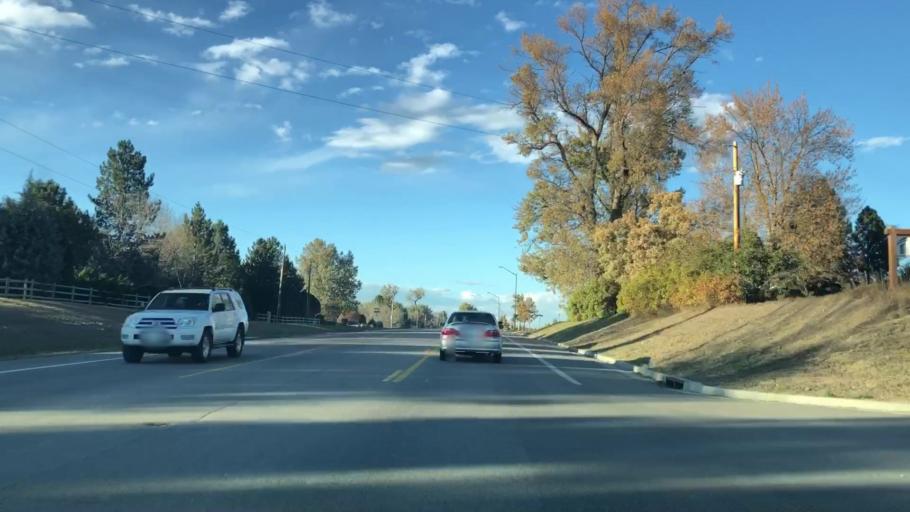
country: US
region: Colorado
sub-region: Larimer County
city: Loveland
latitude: 40.4911
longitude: -105.0393
